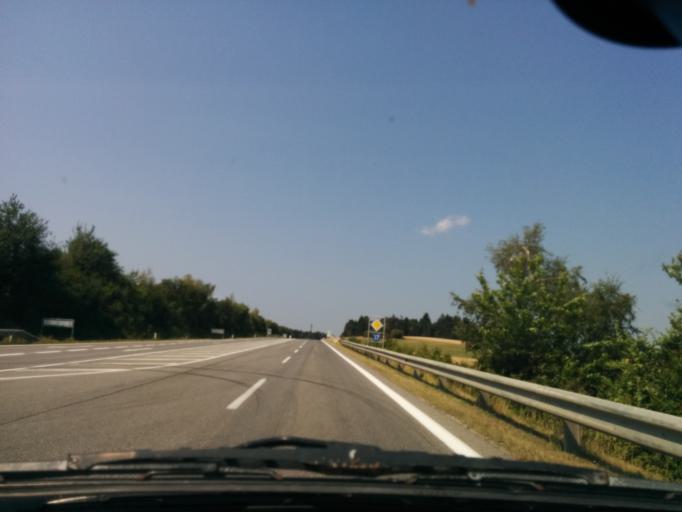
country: AT
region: Lower Austria
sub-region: Politischer Bezirk Krems
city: Rastenfeld
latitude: 48.5373
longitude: 15.3862
